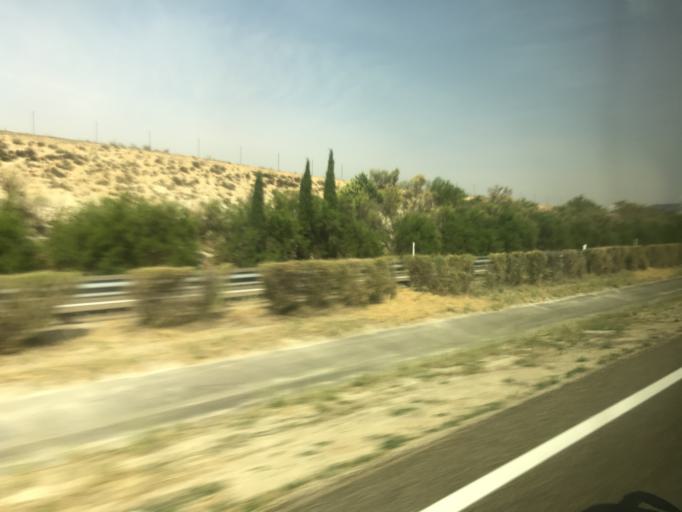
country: ES
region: Castille and Leon
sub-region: Provincia de Palencia
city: Villalobon
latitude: 42.0133
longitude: -4.5029
